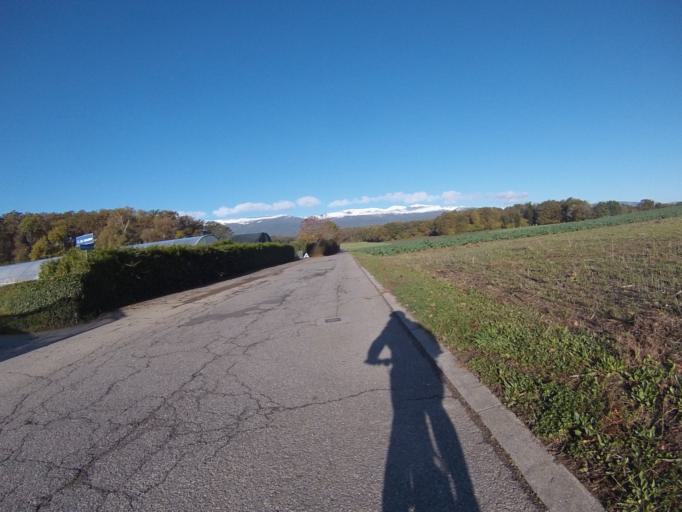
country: CH
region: Geneva
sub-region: Geneva
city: Meyrin
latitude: 46.2381
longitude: 6.0733
